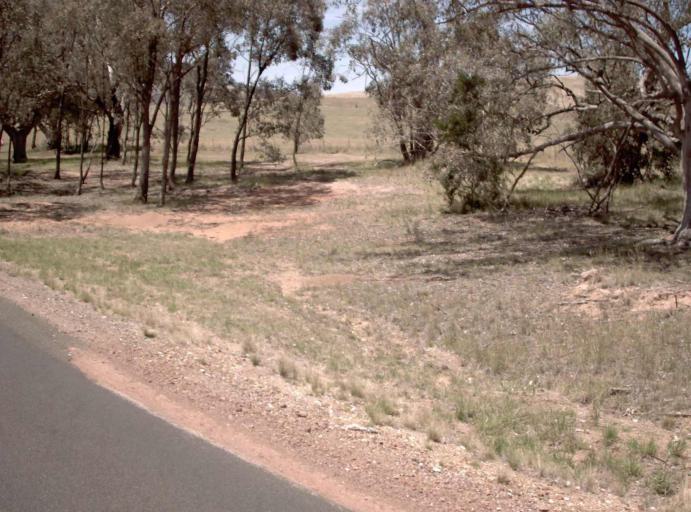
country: AU
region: Victoria
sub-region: East Gippsland
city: Bairnsdale
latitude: -37.1844
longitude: 147.7153
